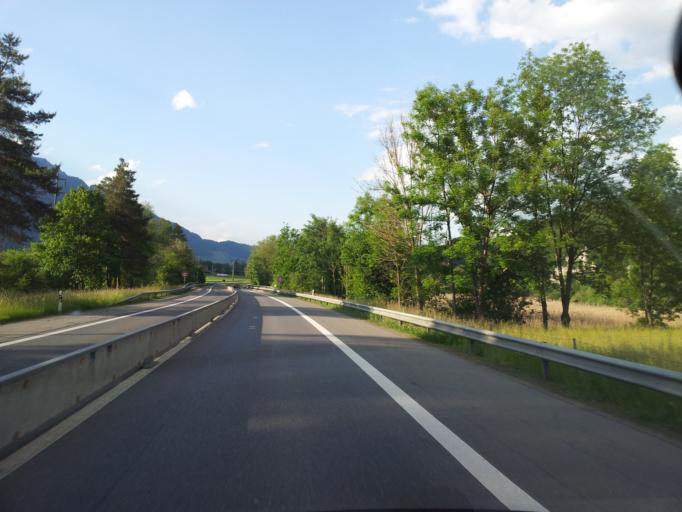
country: CH
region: Obwalden
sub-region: Obwalden
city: Kerns
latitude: 46.9136
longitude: 8.2662
